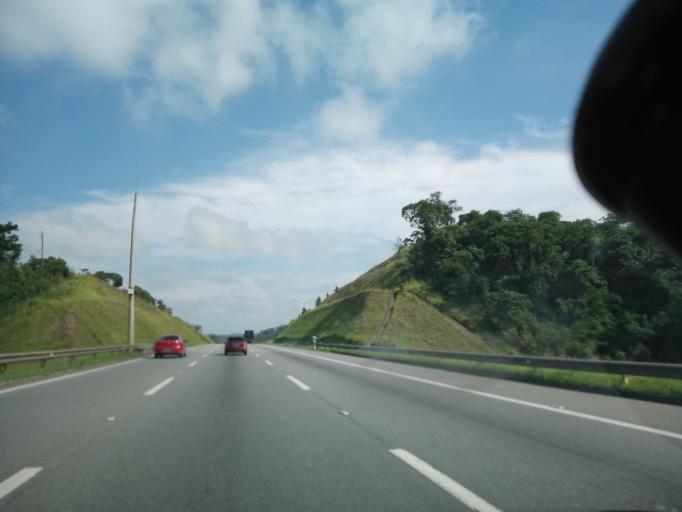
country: BR
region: Sao Paulo
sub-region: Itapecerica Da Serra
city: Itapecerica da Serra
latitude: -23.7106
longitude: -46.8087
